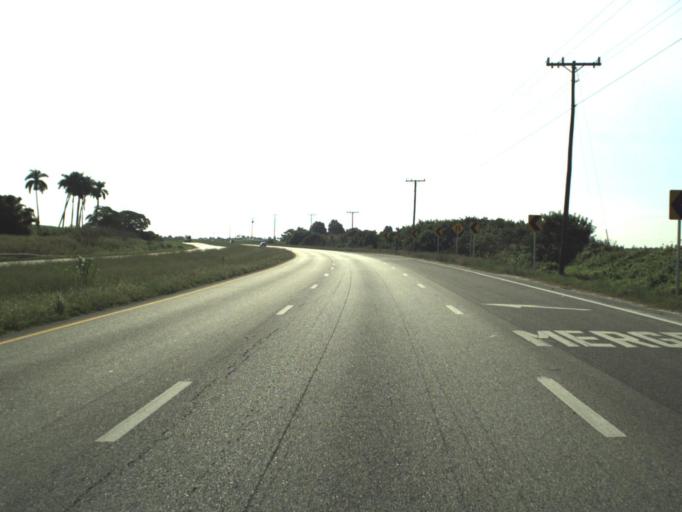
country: US
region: Florida
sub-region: Palm Beach County
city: South Bay
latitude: 26.6814
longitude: -80.7492
